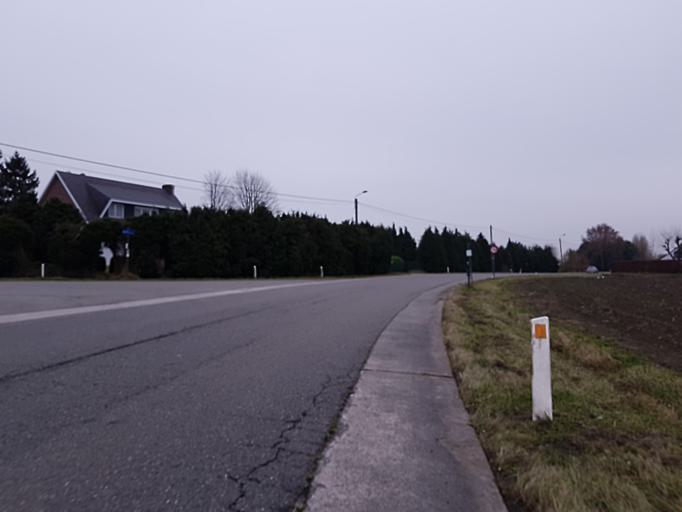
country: BE
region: Flanders
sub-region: Provincie Antwerpen
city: Willebroek
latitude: 51.0408
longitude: 4.3915
